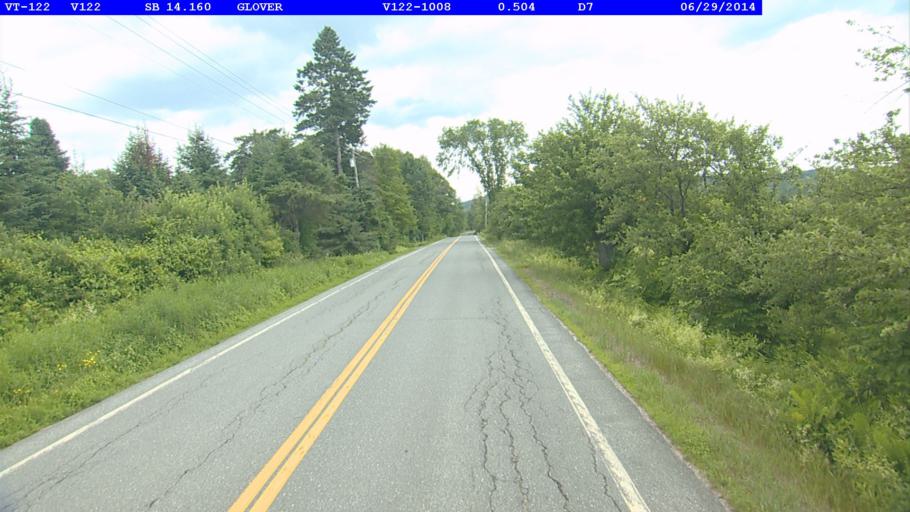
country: US
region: Vermont
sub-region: Caledonia County
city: Lyndonville
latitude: 44.6825
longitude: -72.1724
